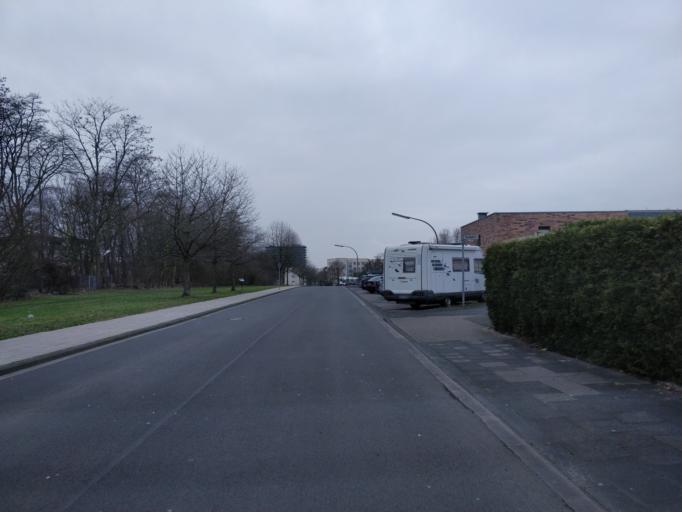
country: DE
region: North Rhine-Westphalia
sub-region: Regierungsbezirk Koln
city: Mengenich
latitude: 50.9765
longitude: 6.8691
